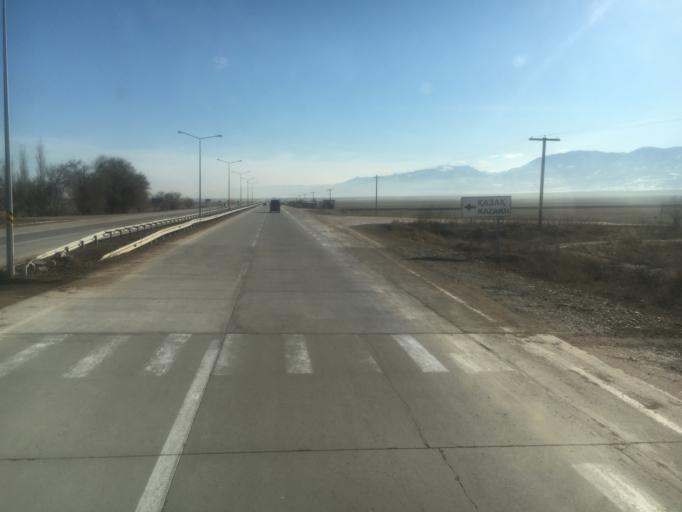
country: KZ
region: Zhambyl
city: Lugovoy
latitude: 42.9061
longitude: 72.9099
